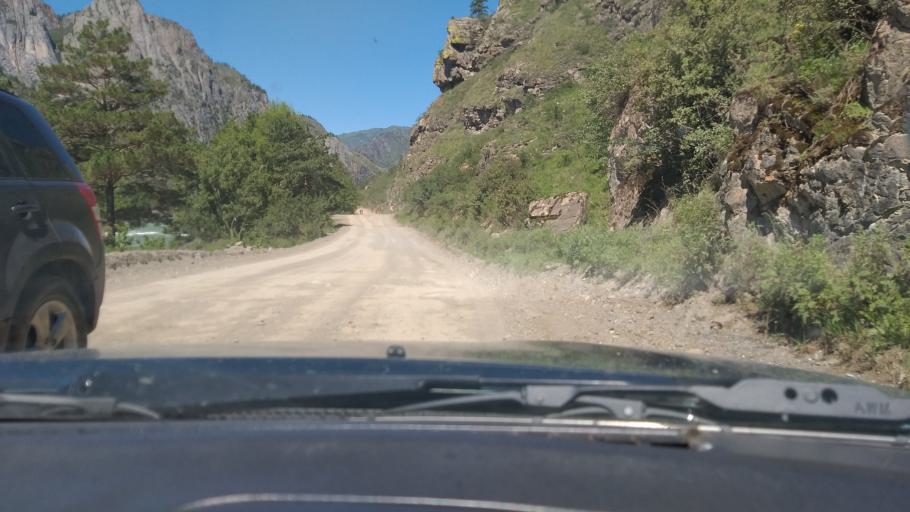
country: RU
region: Altay
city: Chemal
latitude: 51.2007
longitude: 86.0856
